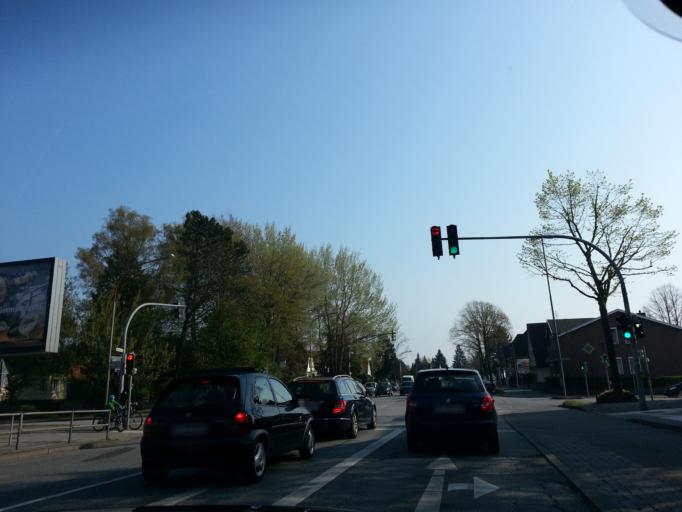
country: DE
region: Schleswig-Holstein
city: Bad Schwartau
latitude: 53.8987
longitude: 10.6901
